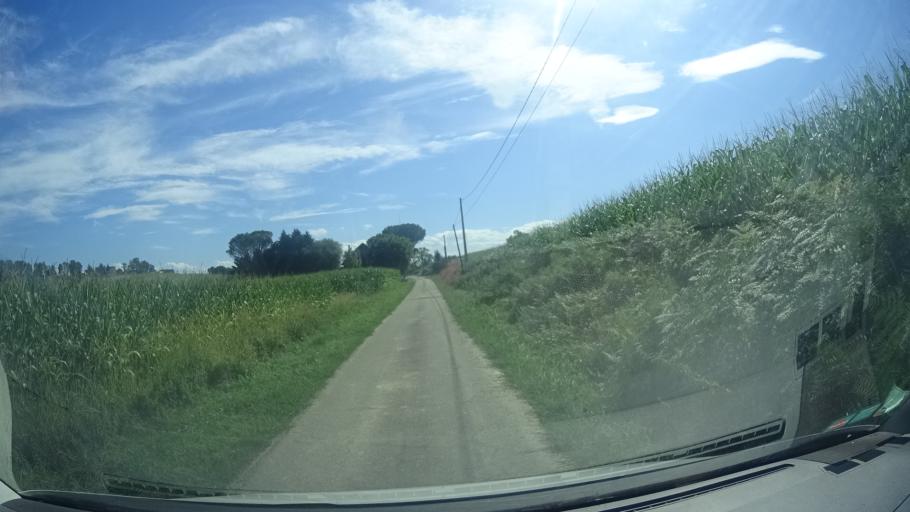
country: FR
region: Aquitaine
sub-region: Departement des Pyrenees-Atlantiques
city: Orthez
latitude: 43.4936
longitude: -0.7099
